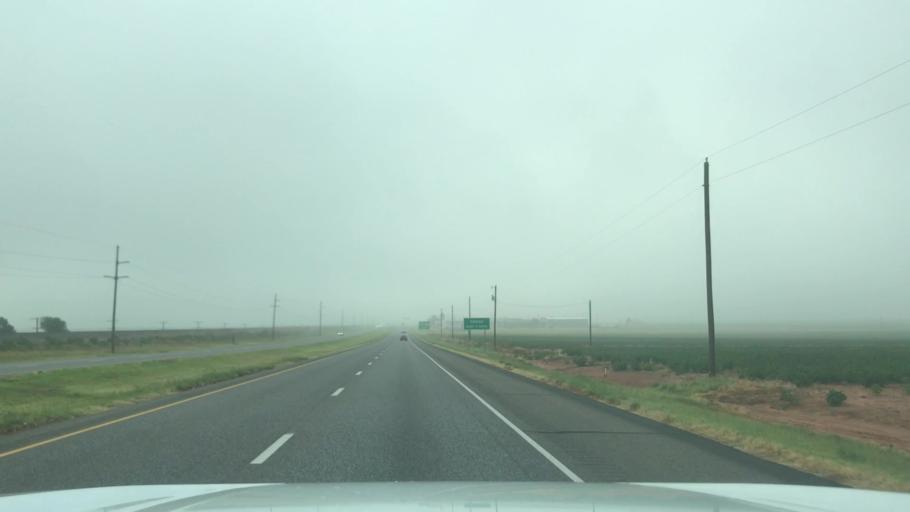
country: US
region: Texas
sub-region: Lubbock County
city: Slaton
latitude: 33.4684
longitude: -101.6854
